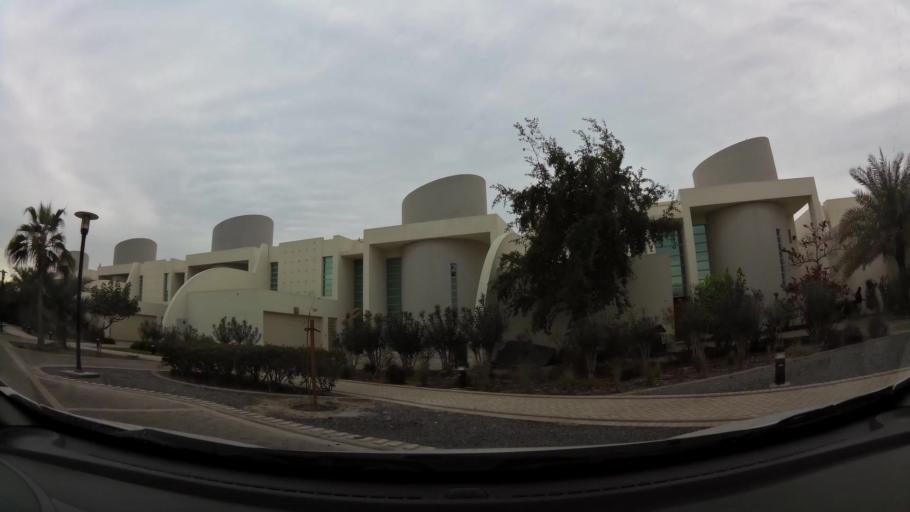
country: BH
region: Central Governorate
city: Dar Kulayb
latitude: 25.8348
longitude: 50.6190
